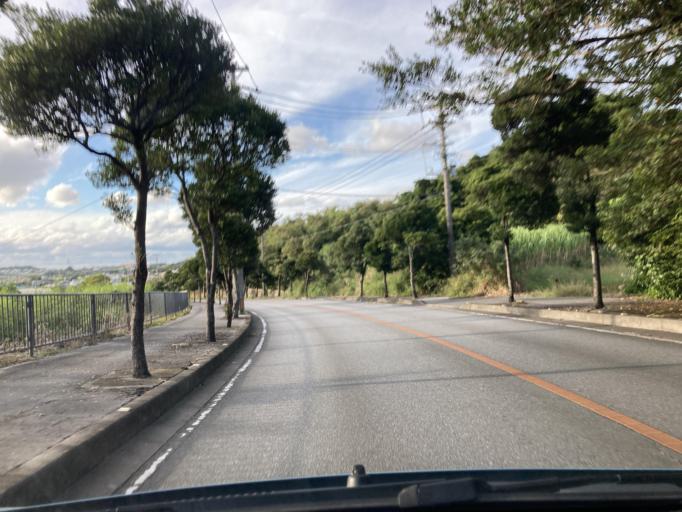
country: JP
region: Okinawa
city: Itoman
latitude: 26.1342
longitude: 127.7224
